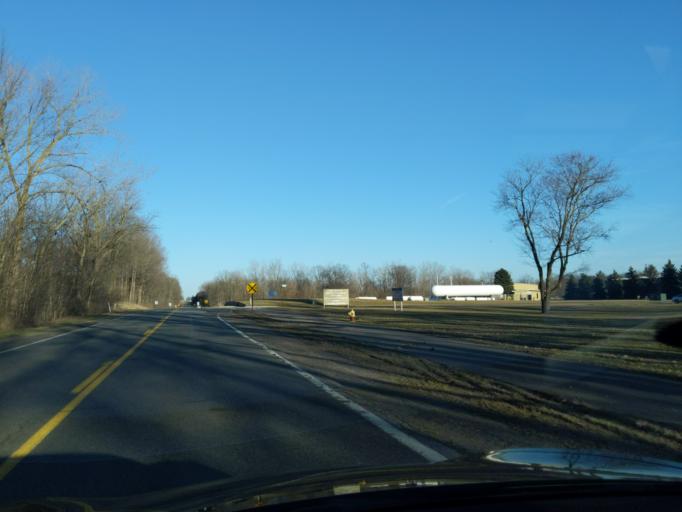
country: US
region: Michigan
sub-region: Ingham County
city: Mason
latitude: 42.5966
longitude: -84.4579
